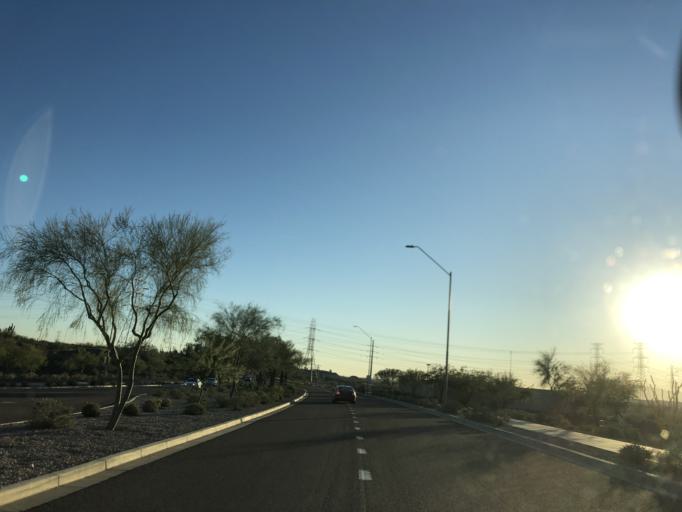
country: US
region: Arizona
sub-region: Maricopa County
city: Sun City West
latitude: 33.7086
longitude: -112.2888
